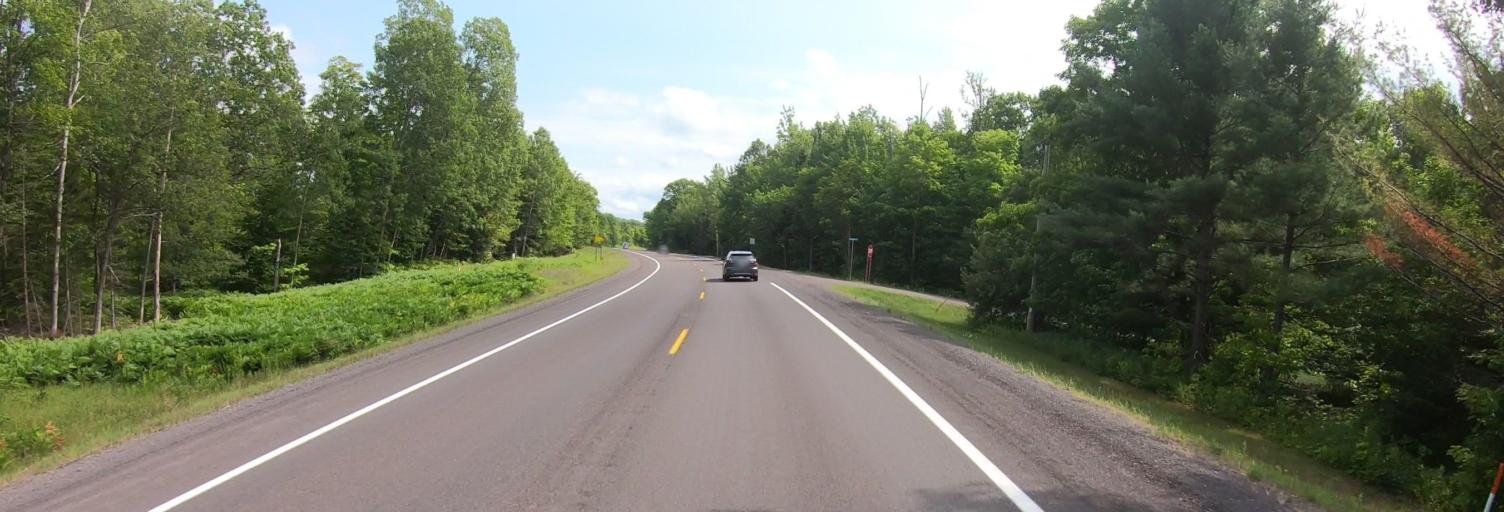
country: US
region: Michigan
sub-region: Houghton County
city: Hancock
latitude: 46.9710
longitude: -88.7798
